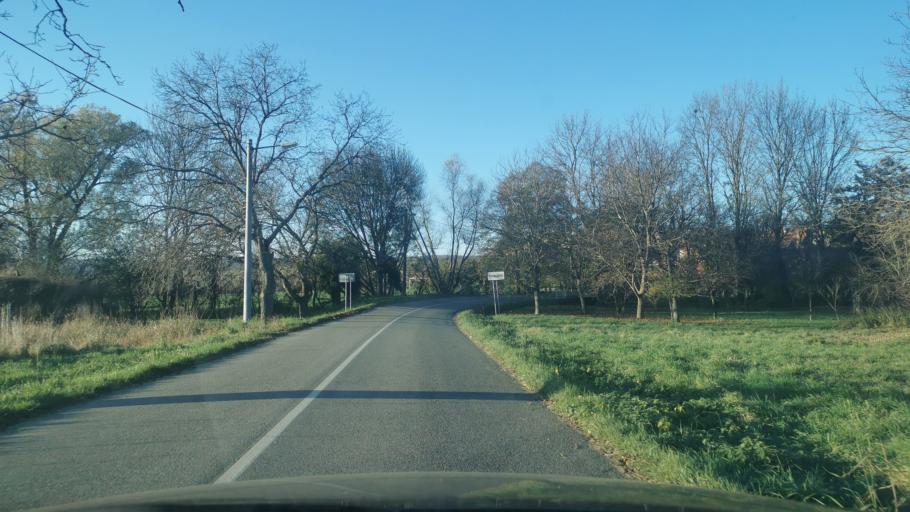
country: CZ
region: South Moravian
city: Sudomerice
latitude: 48.7827
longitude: 17.2996
